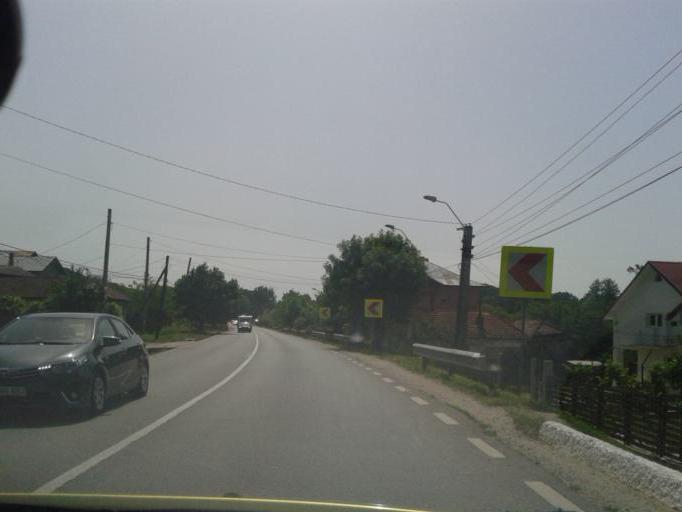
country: RO
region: Arges
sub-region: Comuna Babana
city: Babana
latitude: 44.8947
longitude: 24.7428
